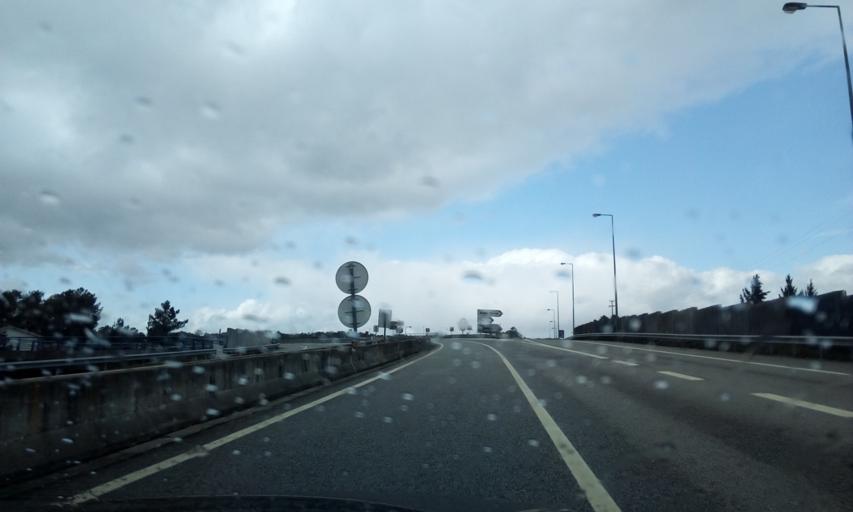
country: PT
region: Viseu
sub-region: Viseu
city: Rio de Loba
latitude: 40.6521
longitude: -7.8615
